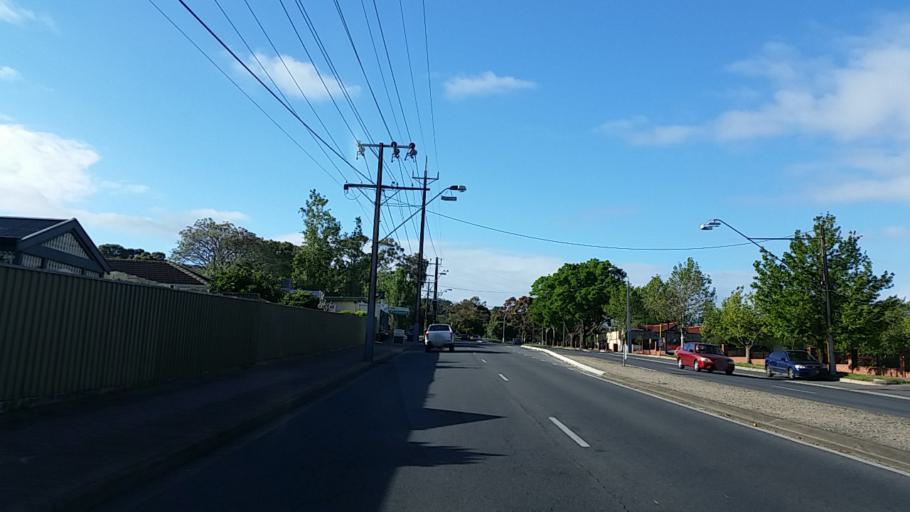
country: AU
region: South Australia
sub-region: Mitcham
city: Clapham
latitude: -34.9974
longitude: 138.5932
